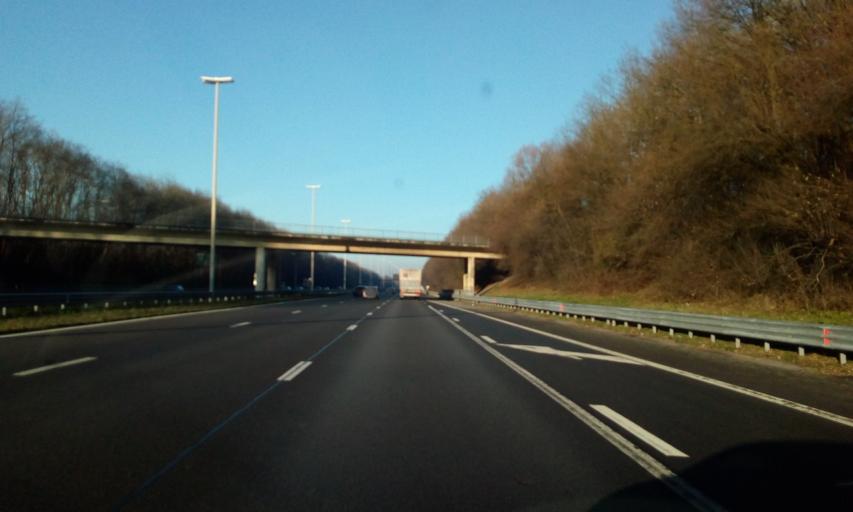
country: BE
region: Wallonia
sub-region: Province du Brabant Wallon
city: Nivelles
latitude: 50.6324
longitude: 4.3075
